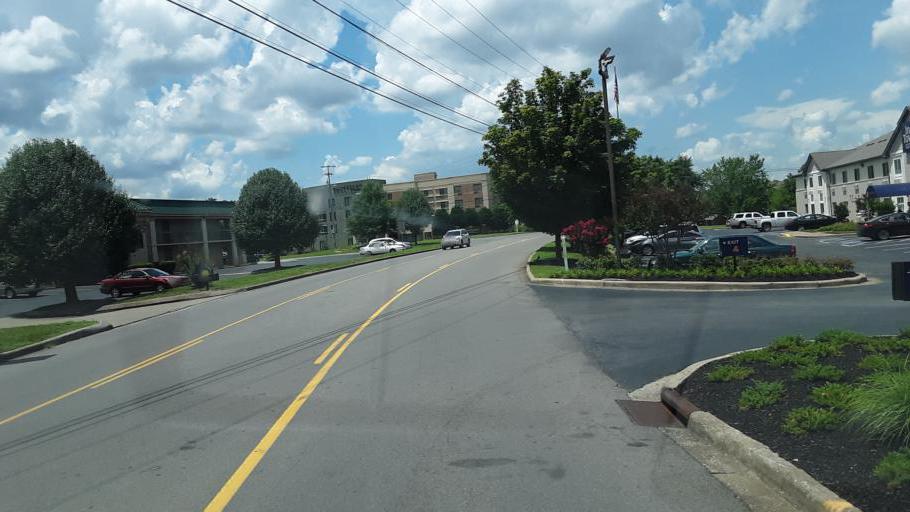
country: US
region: Tennessee
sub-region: Montgomery County
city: Clarksville
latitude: 36.5978
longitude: -87.2877
